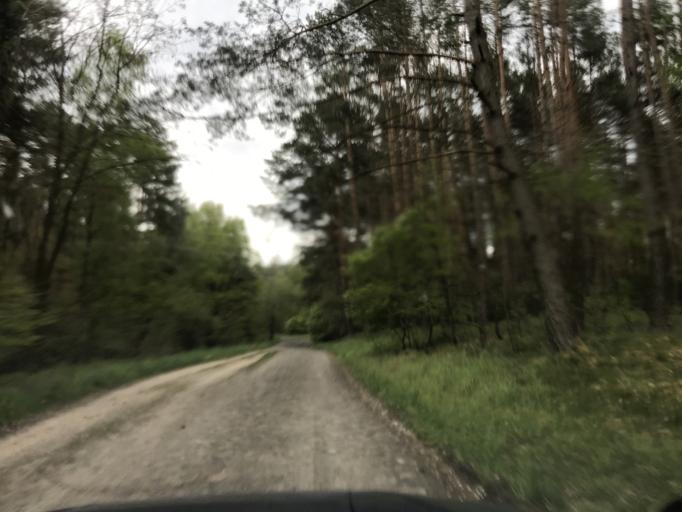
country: PL
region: West Pomeranian Voivodeship
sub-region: Powiat mysliborski
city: Mysliborz
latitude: 52.8706
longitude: 14.8825
